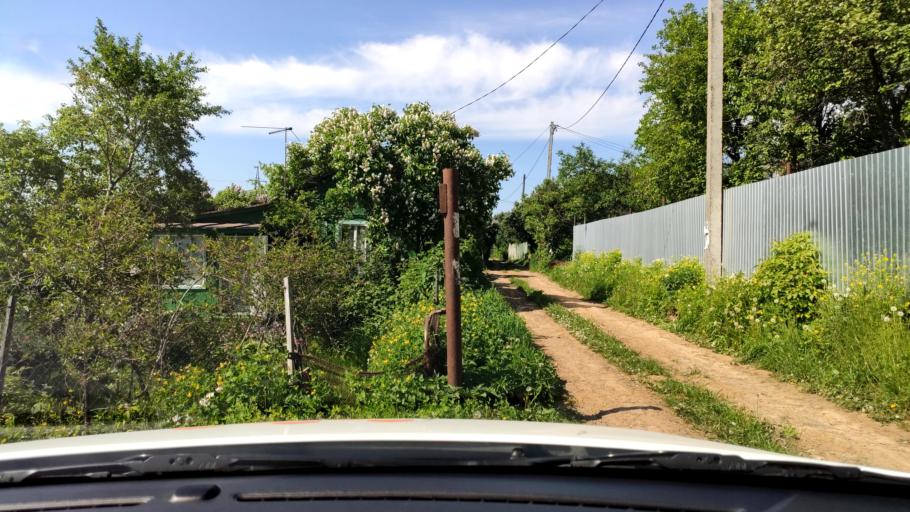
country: RU
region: Tatarstan
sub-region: Gorod Kazan'
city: Kazan
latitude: 55.8197
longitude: 49.2113
